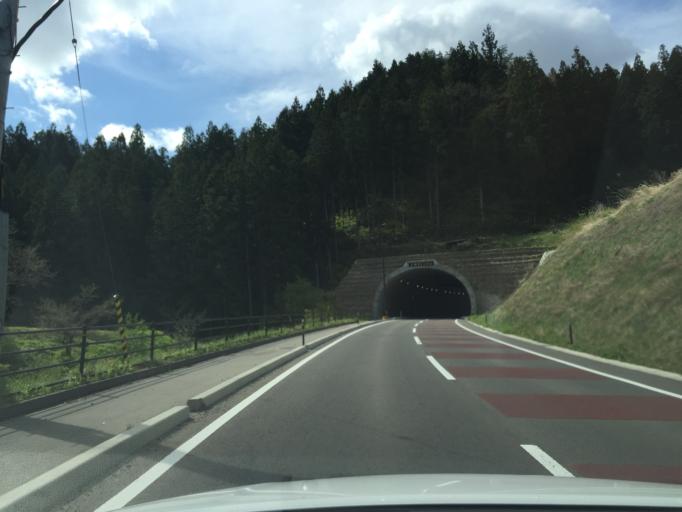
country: JP
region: Fukushima
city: Hobaramachi
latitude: 37.6389
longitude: 140.6435
